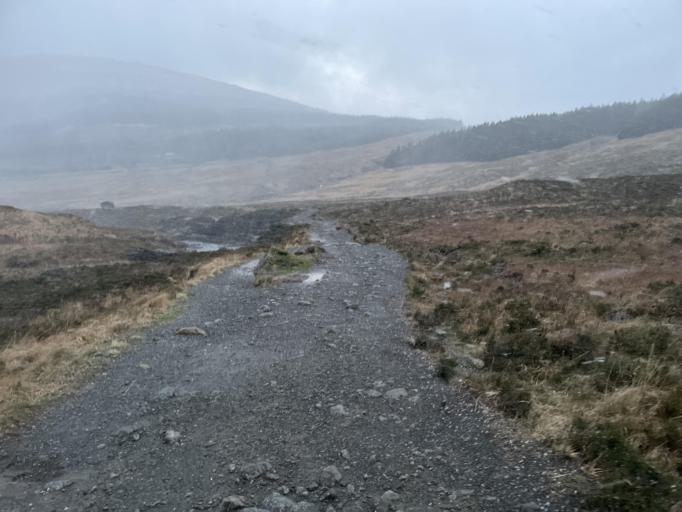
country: GB
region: Scotland
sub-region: Highland
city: Isle of Skye
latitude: 57.2498
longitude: -6.2626
